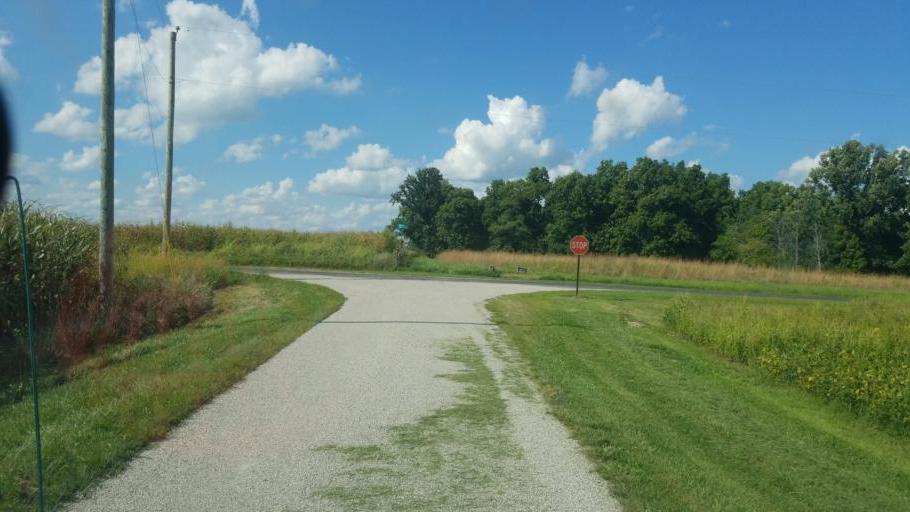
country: US
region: Ohio
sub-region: Union County
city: Richwood
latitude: 40.5132
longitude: -83.3711
